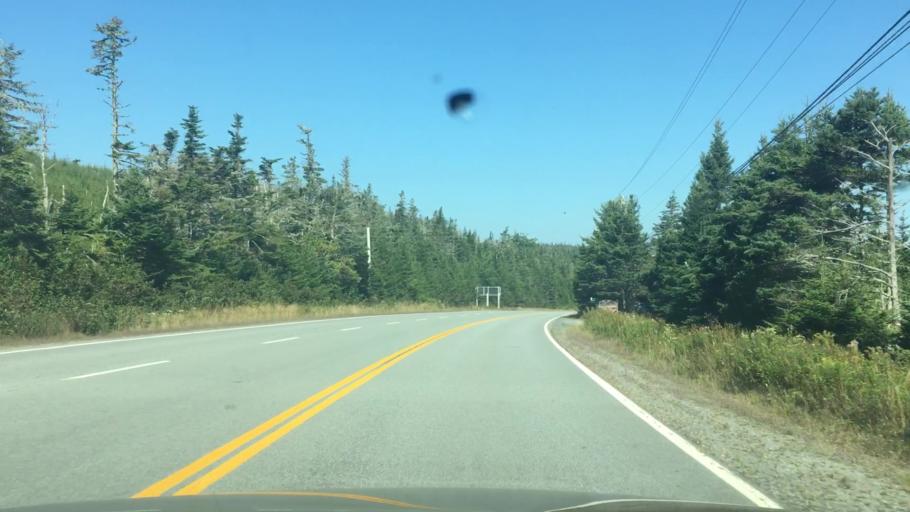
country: CA
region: Nova Scotia
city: New Glasgow
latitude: 44.8179
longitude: -62.6331
